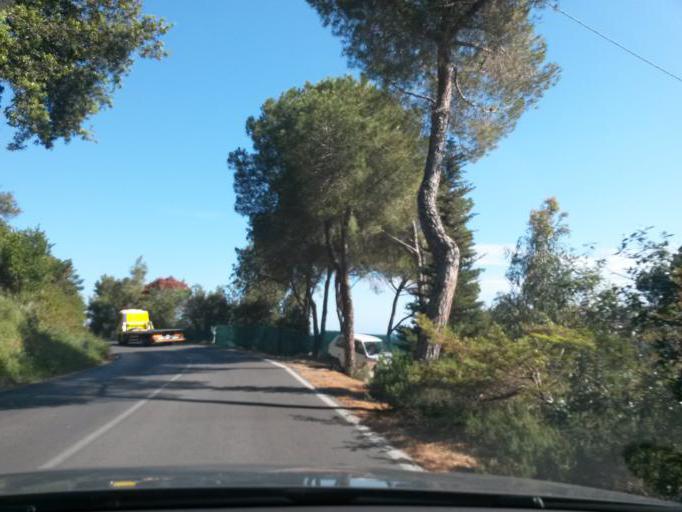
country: IT
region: Tuscany
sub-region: Provincia di Livorno
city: Marciana Marina
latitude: 42.8028
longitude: 10.2100
